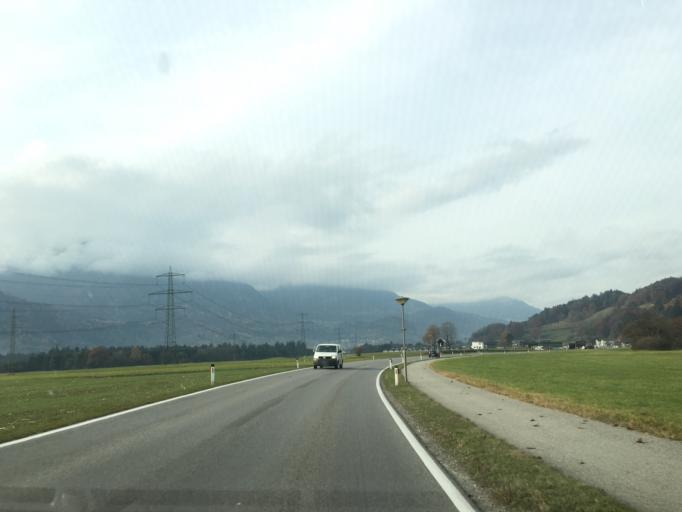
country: AT
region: Vorarlberg
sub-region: Politischer Bezirk Bludenz
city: Bludesch
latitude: 47.1962
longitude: 9.7365
